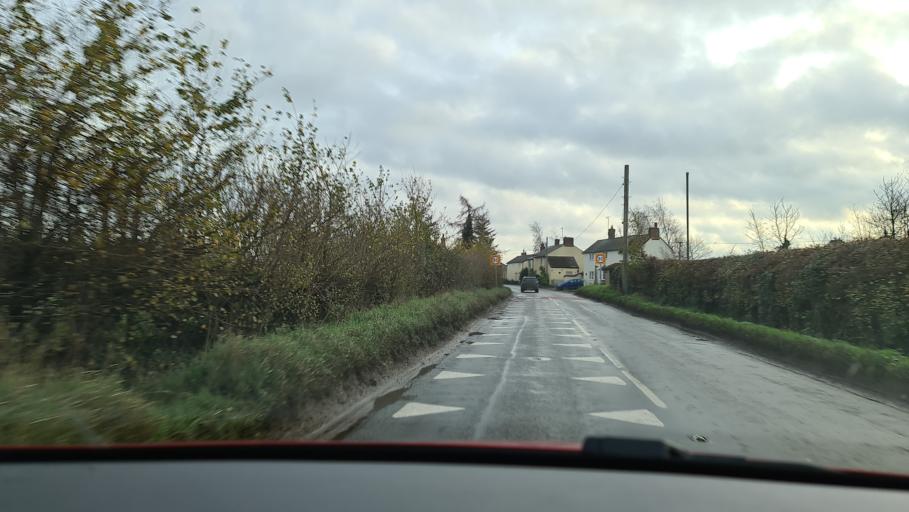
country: GB
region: England
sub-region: Buckinghamshire
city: Haddenham
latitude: 51.7932
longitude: -0.9348
